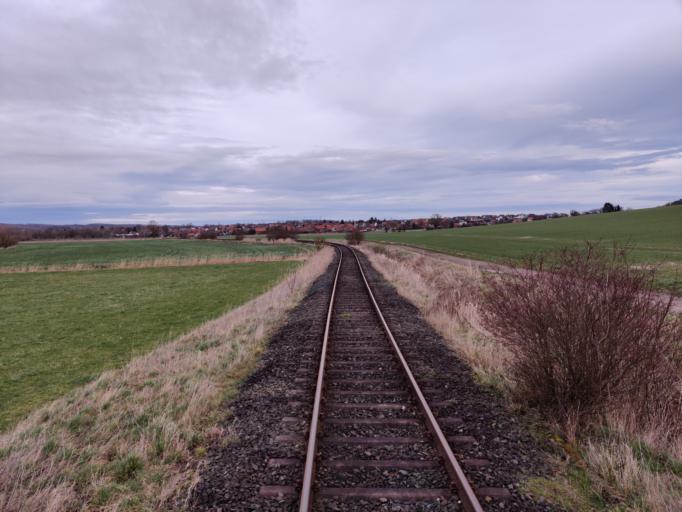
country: DE
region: Lower Saxony
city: Holle
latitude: 52.0760
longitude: 10.1527
